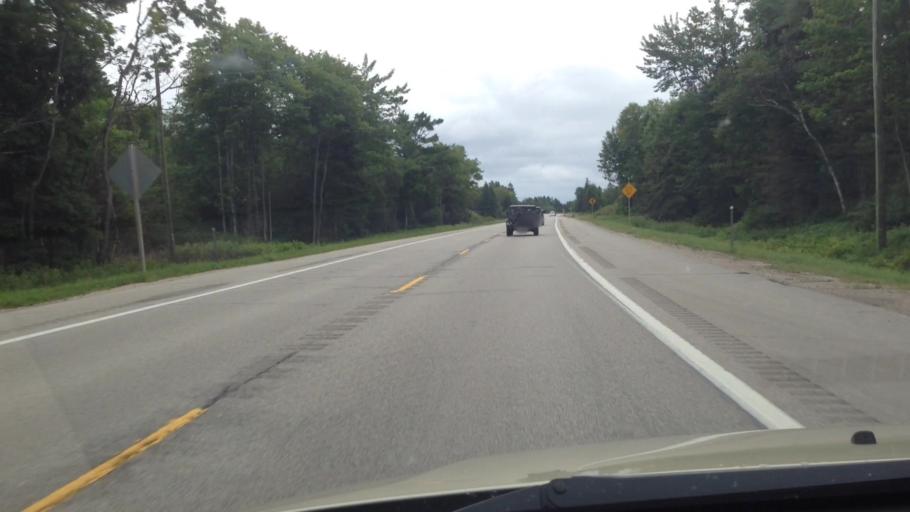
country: US
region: Michigan
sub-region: Luce County
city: Newberry
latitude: 46.0972
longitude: -85.4774
